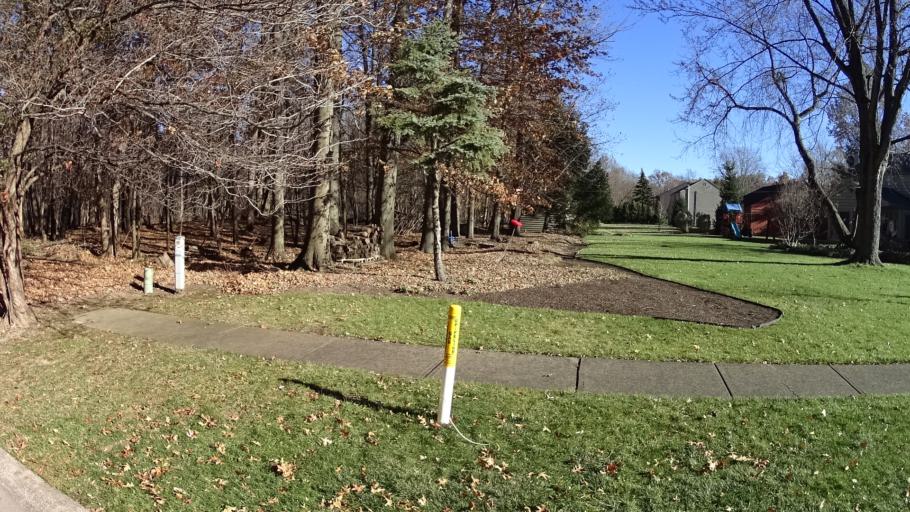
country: US
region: Ohio
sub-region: Lorain County
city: Avon Lake
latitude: 41.4966
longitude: -82.0159
